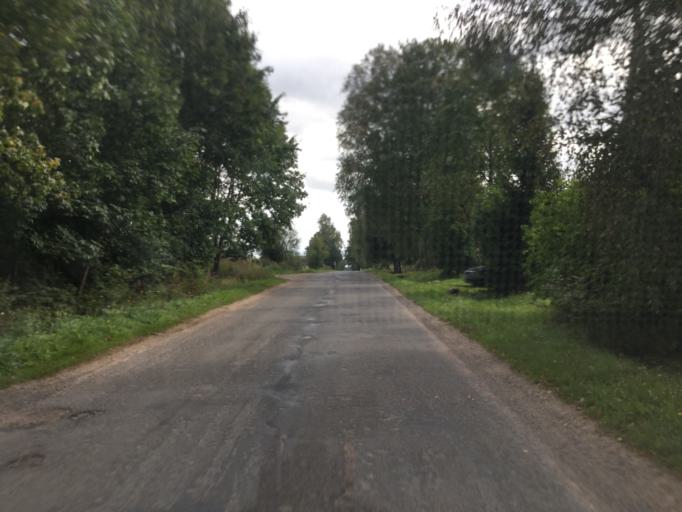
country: BY
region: Vitebsk
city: Vitebsk
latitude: 55.1467
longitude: 30.2818
